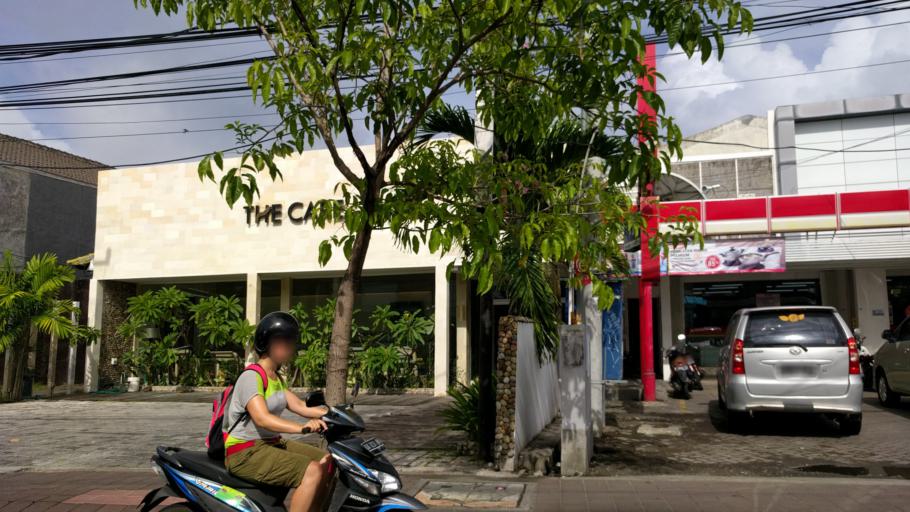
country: ID
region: Bali
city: Kuta
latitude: -8.6805
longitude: 115.1645
